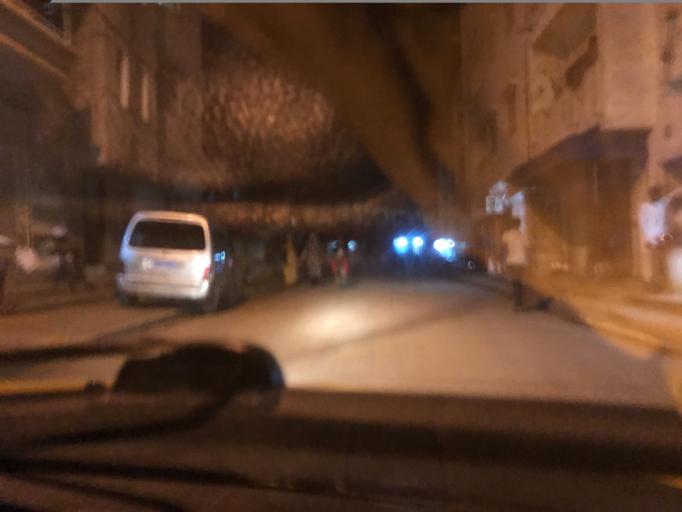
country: SN
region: Dakar
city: Grand Dakar
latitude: 14.7529
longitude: -17.4498
